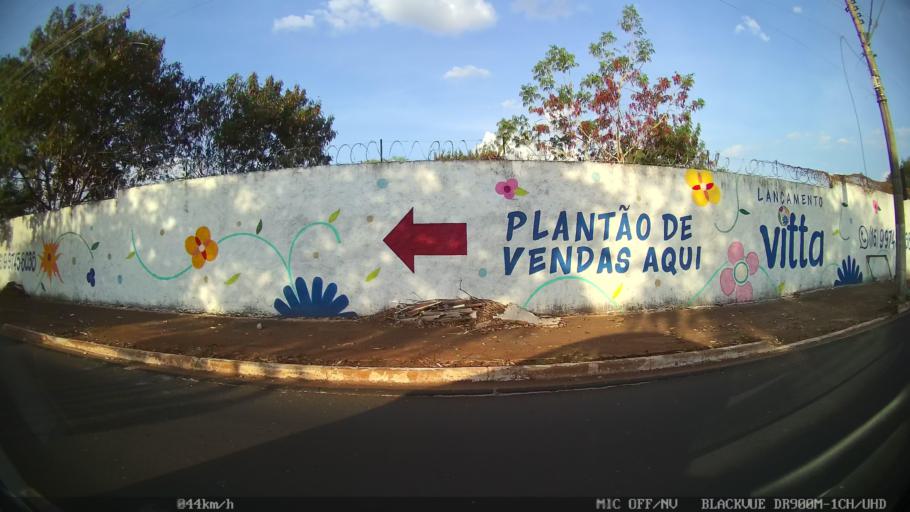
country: BR
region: Sao Paulo
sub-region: Ribeirao Preto
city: Ribeirao Preto
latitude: -21.1292
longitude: -47.8029
